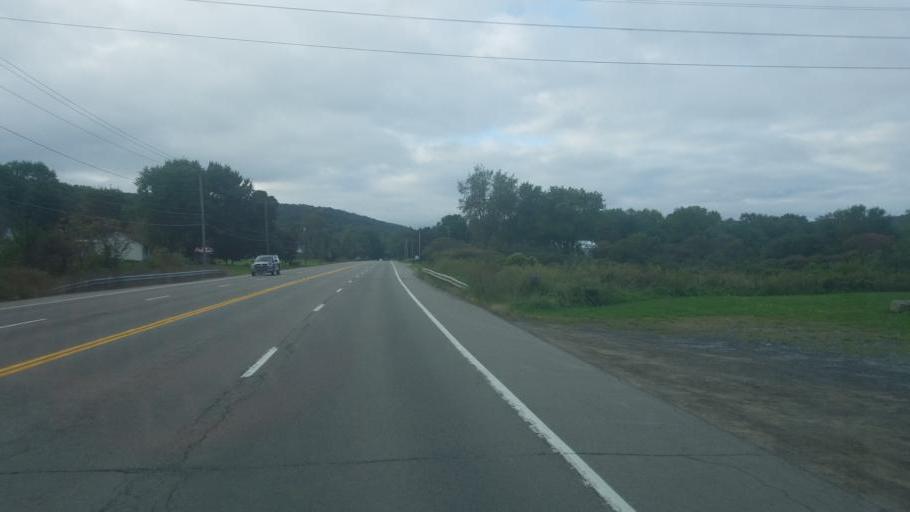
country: US
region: New York
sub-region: Cattaraugus County
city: Olean
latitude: 42.1428
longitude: -78.4004
